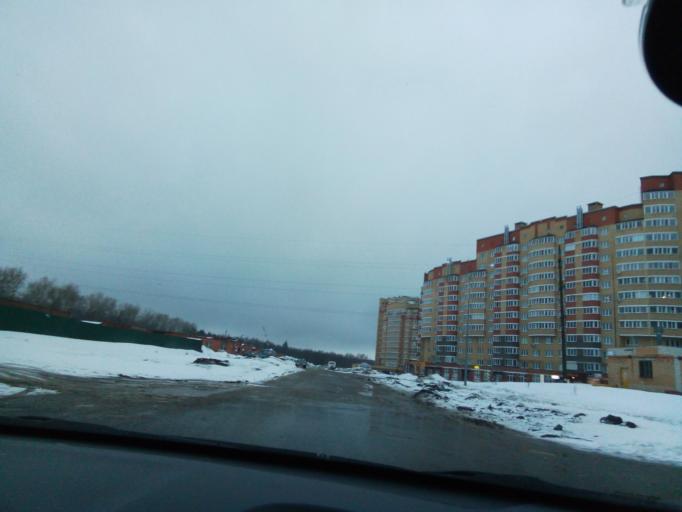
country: RU
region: Chuvashia
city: Novyye Lapsary
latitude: 56.1317
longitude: 47.1538
